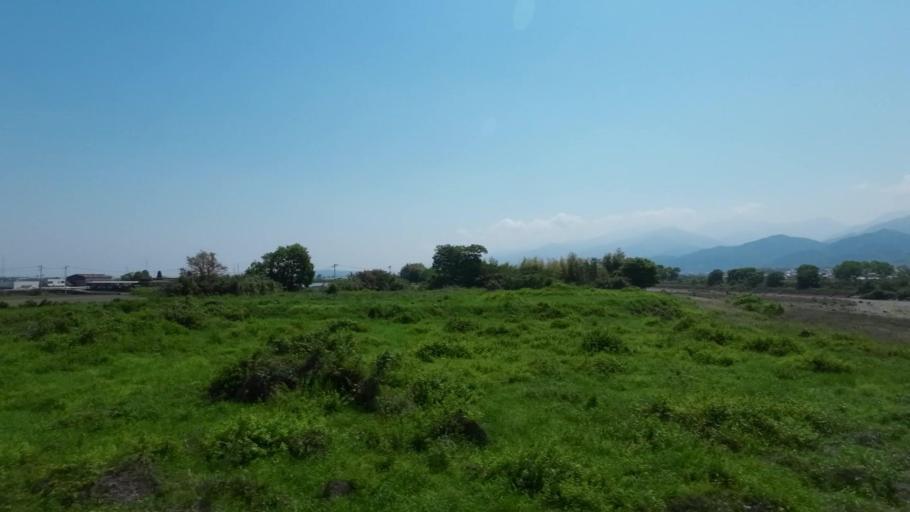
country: JP
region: Ehime
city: Saijo
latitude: 33.9069
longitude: 133.0993
